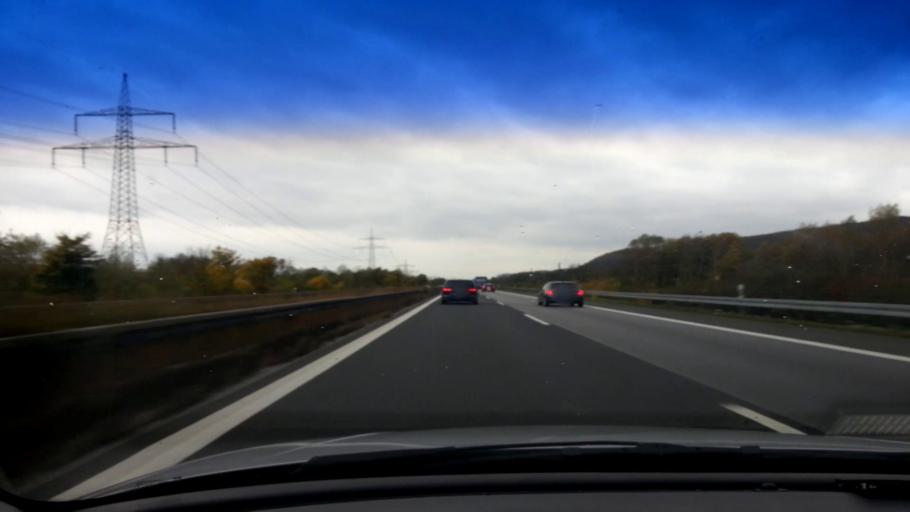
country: DE
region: Bavaria
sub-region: Regierungsbezirk Unterfranken
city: Stettfeld
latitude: 49.9716
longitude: 10.7037
